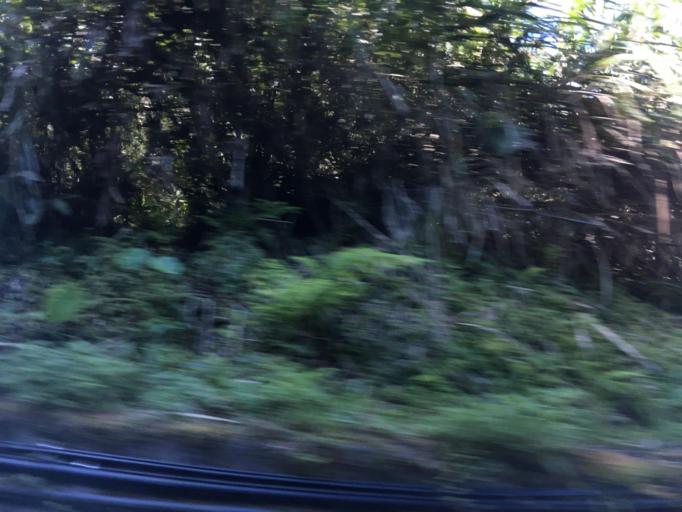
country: TW
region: Taiwan
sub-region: Yilan
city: Yilan
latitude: 24.5431
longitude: 121.5118
